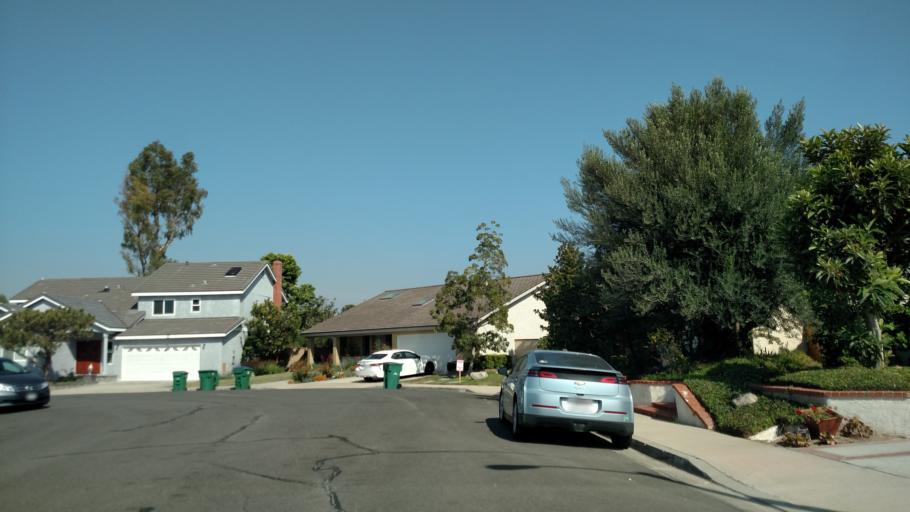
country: US
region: California
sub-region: Orange County
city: Irvine
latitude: 33.6907
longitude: -117.7905
